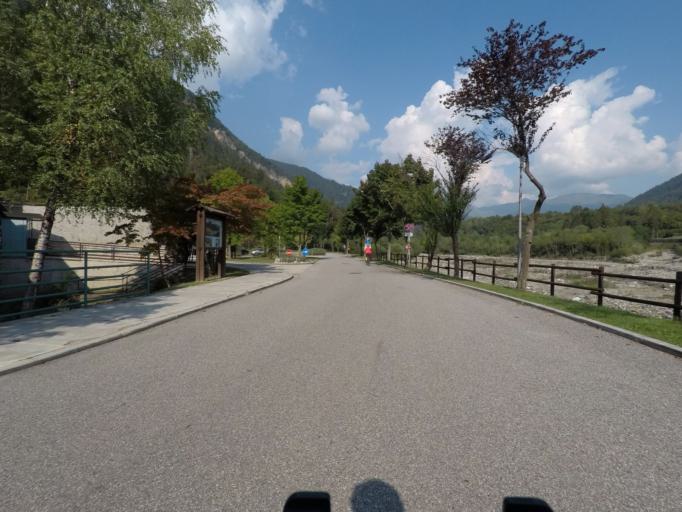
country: IT
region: Friuli Venezia Giulia
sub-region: Provincia di Udine
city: Arta Terme
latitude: 46.4770
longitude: 13.0176
